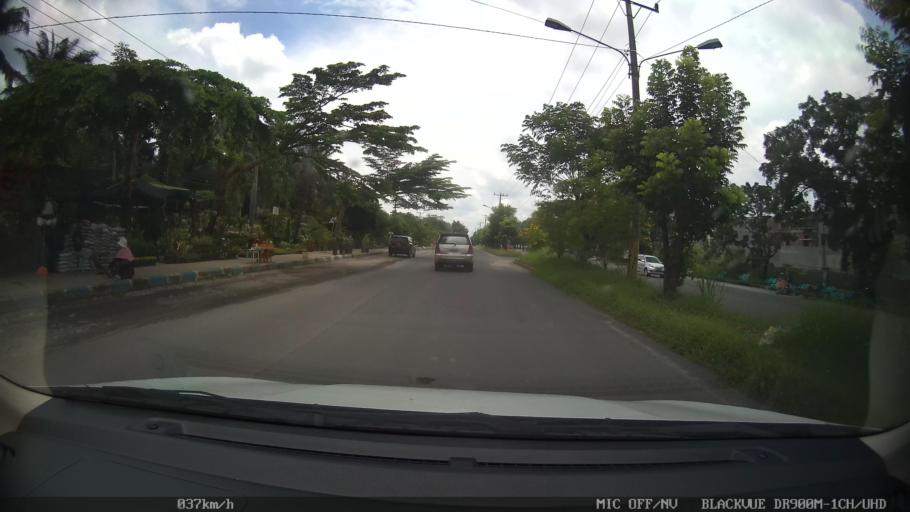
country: ID
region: North Sumatra
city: Medan
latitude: 3.6127
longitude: 98.7123
